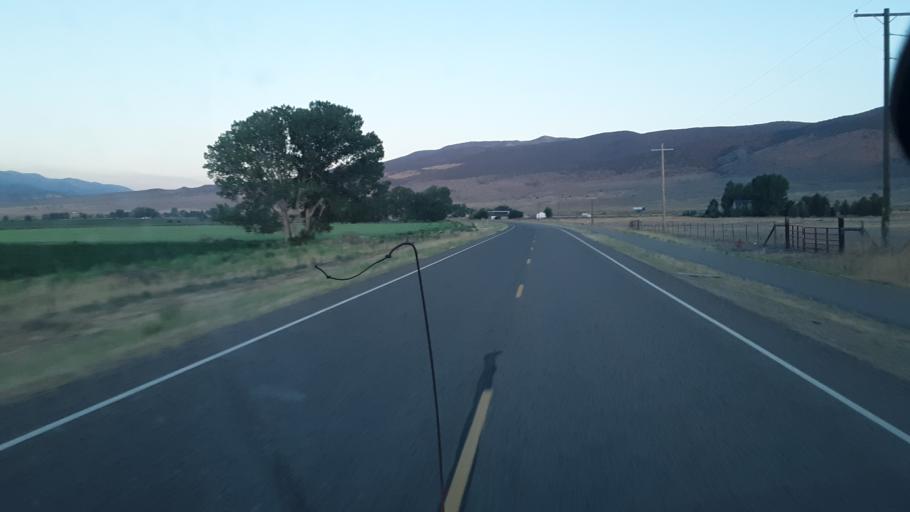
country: US
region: Utah
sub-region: Sevier County
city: Monroe
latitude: 38.6536
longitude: -112.1984
